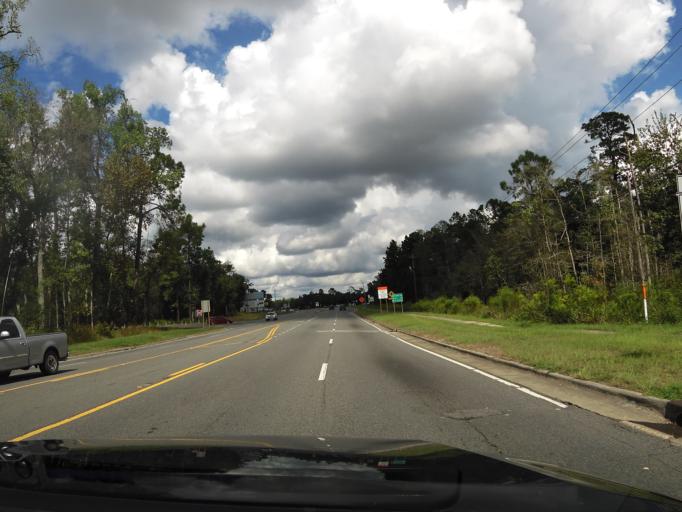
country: US
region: Georgia
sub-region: Charlton County
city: Folkston
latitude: 30.8375
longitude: -82.0070
